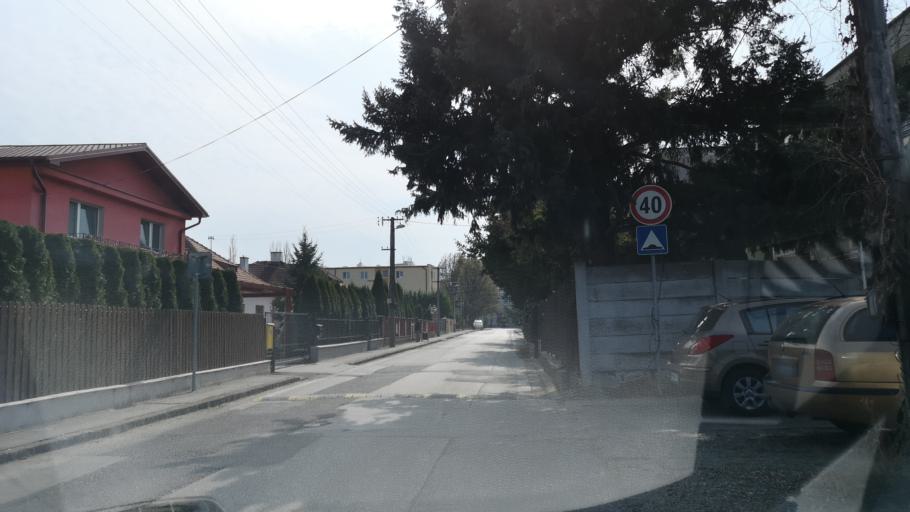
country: SK
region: Nitriansky
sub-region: Okres Nitra
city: Nitra
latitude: 48.3121
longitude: 18.0739
